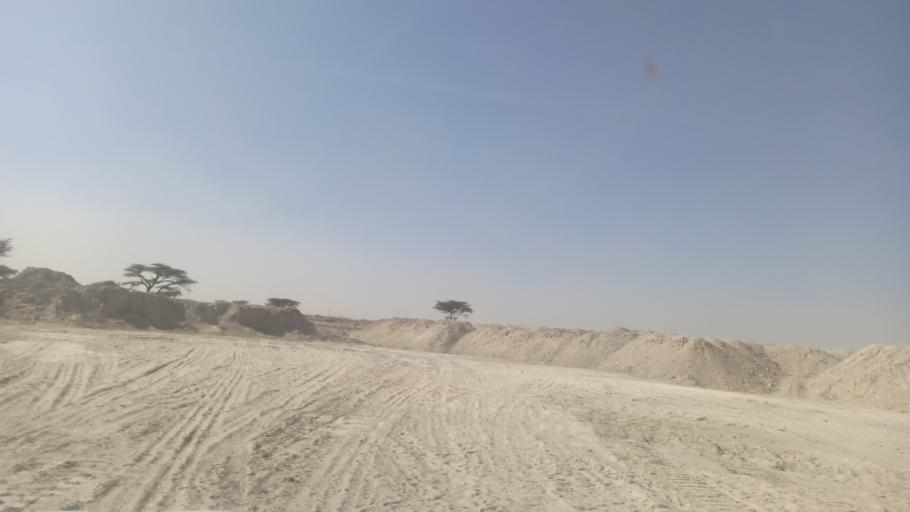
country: ET
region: Oromiya
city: Ziway
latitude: 7.6915
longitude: 38.6632
